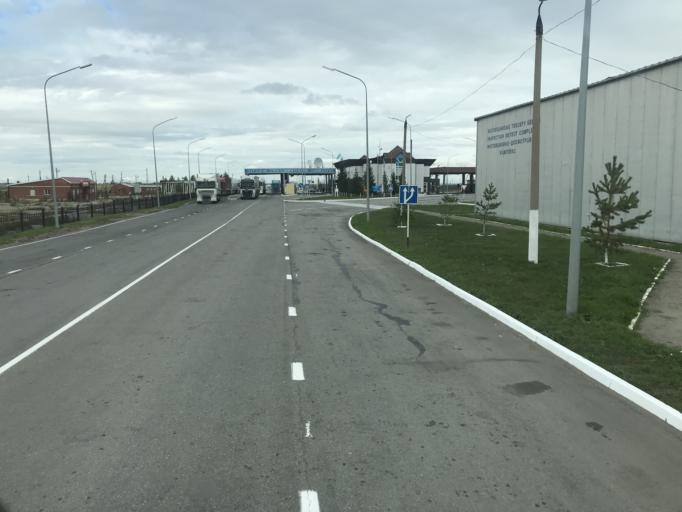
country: RU
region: Chelyabinsk
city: Bobrovka
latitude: 53.9995
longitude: 61.6403
